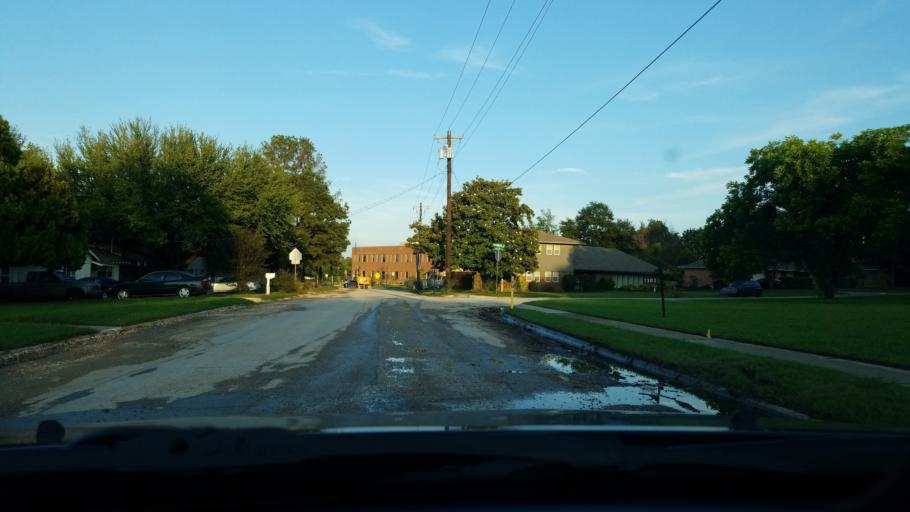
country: US
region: Texas
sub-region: Denton County
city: Denton
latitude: 33.2432
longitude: -97.1159
